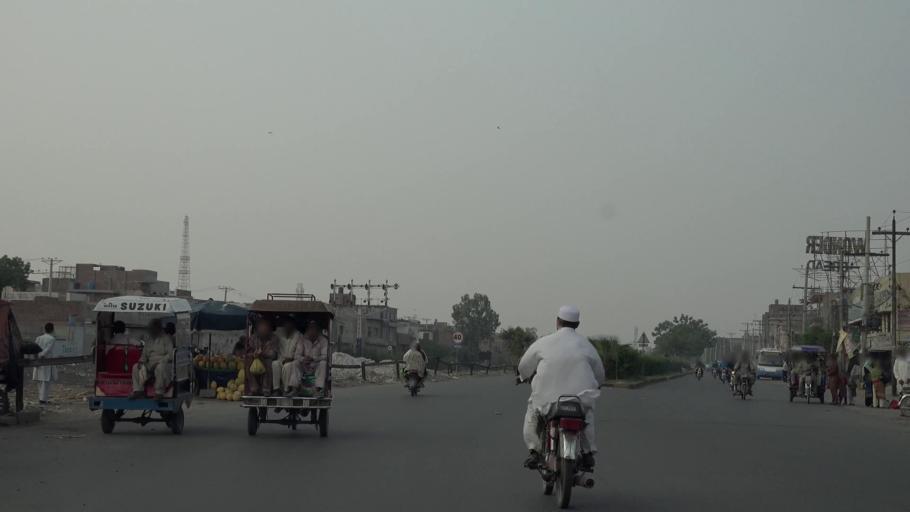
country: PK
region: Punjab
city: Faisalabad
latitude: 31.4209
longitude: 73.1030
